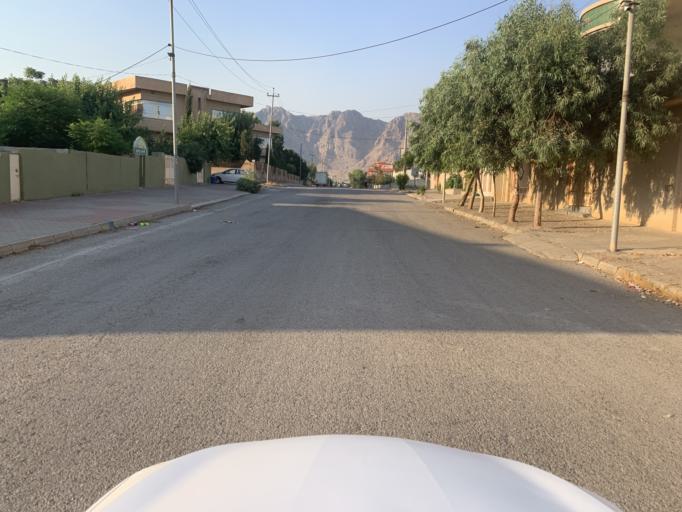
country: IQ
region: As Sulaymaniyah
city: Raniye
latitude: 36.2414
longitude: 44.8784
